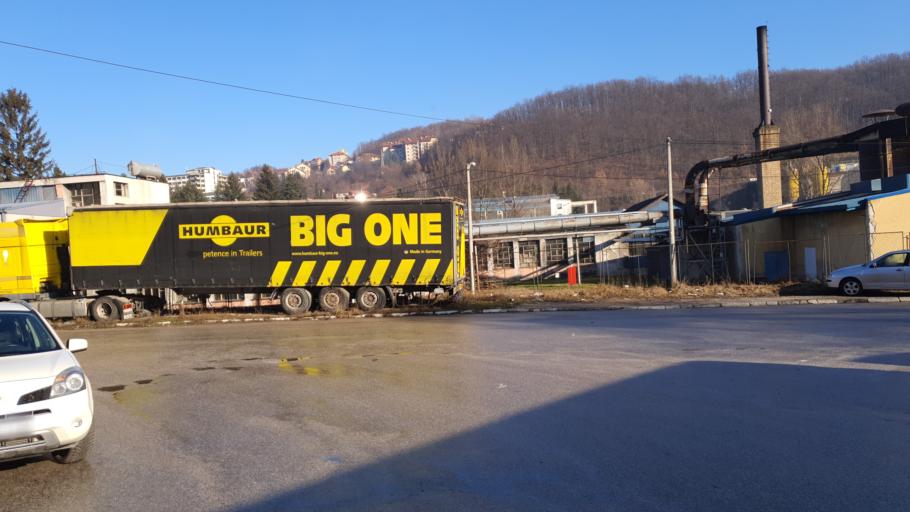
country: RS
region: Central Serbia
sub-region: Zlatiborski Okrug
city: Uzice
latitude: 43.8473
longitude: 19.8596
